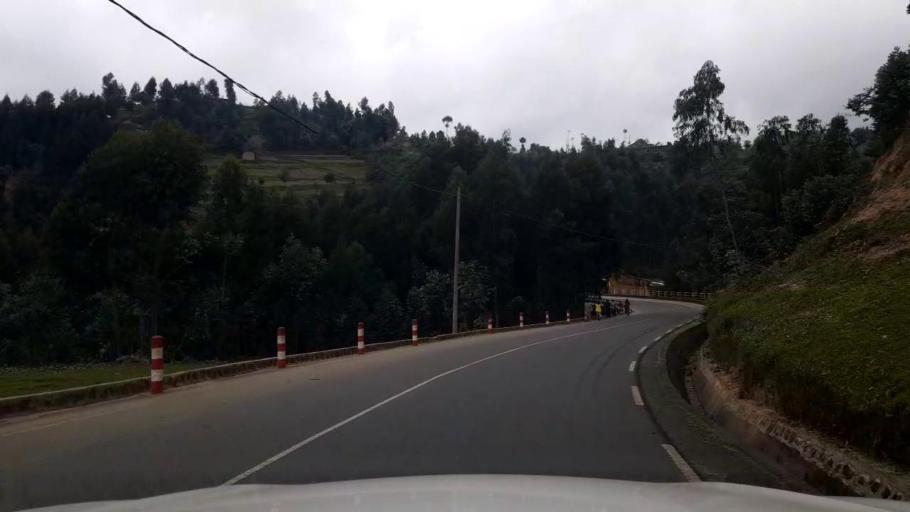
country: RW
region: Northern Province
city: Musanze
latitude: -1.6503
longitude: 29.5077
